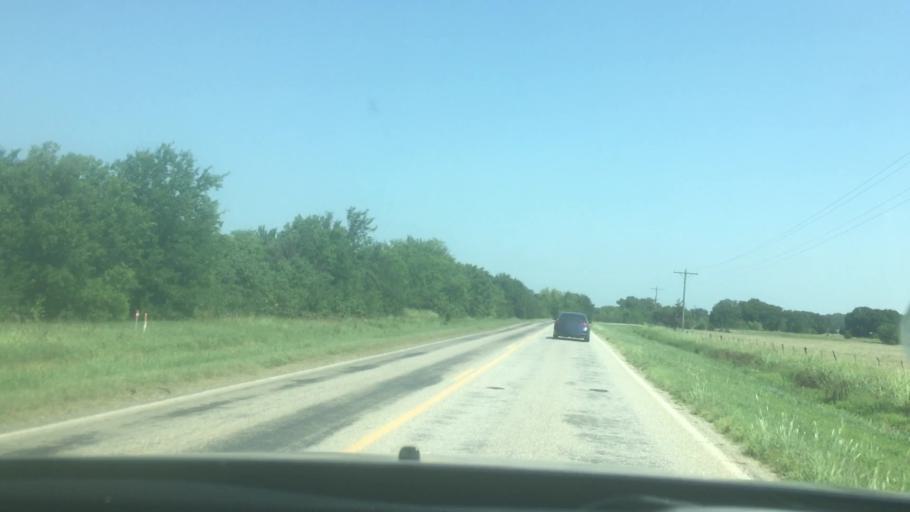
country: US
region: Oklahoma
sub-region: Johnston County
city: Tishomingo
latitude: 34.3485
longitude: -96.4239
